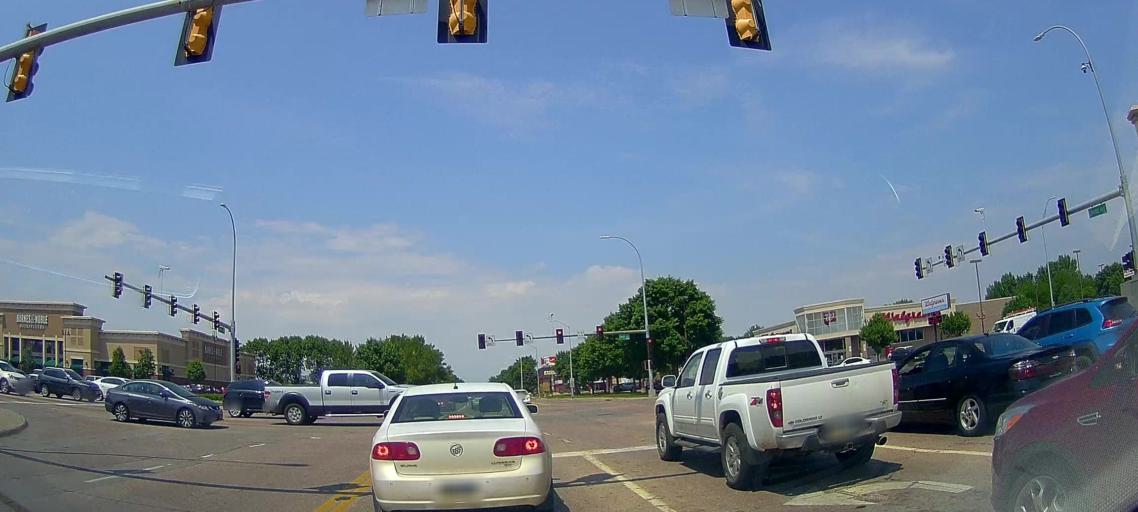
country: US
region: South Dakota
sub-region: Minnehaha County
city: Sioux Falls
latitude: 43.5146
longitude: -96.7711
